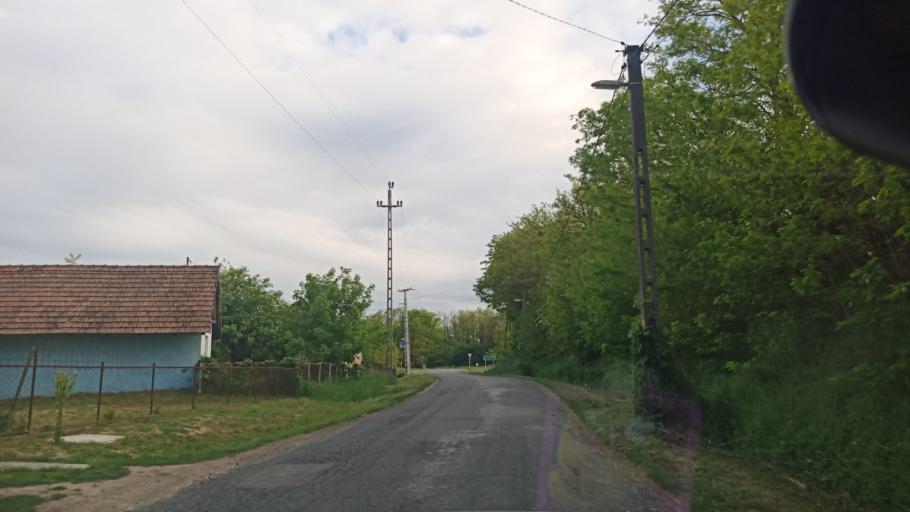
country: HU
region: Zala
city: Pacsa
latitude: 46.7284
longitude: 17.0033
